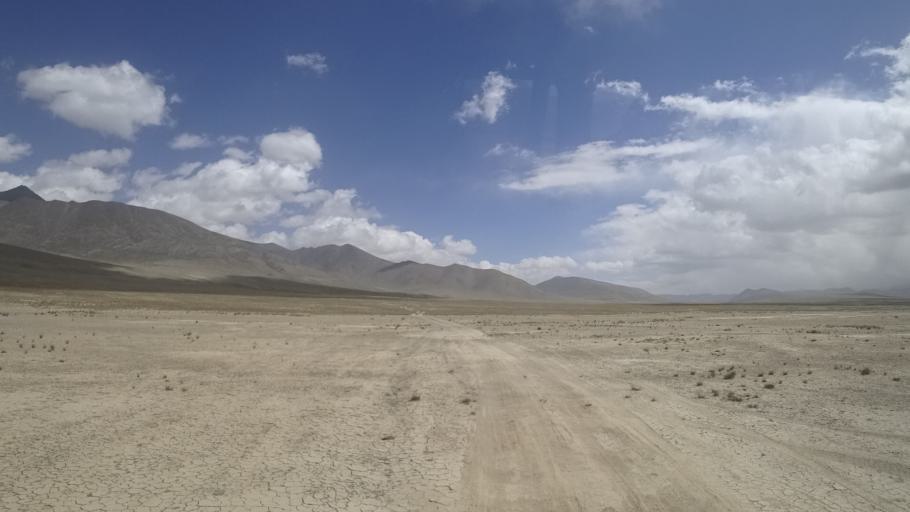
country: TJ
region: Gorno-Badakhshan
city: Murghob
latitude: 37.4779
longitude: 73.9768
